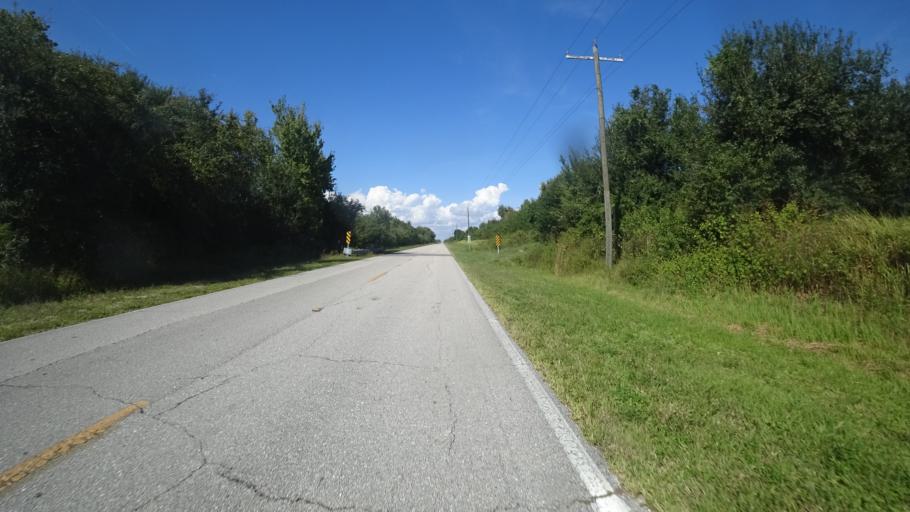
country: US
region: Florida
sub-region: Sarasota County
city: The Meadows
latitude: 27.4338
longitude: -82.2707
